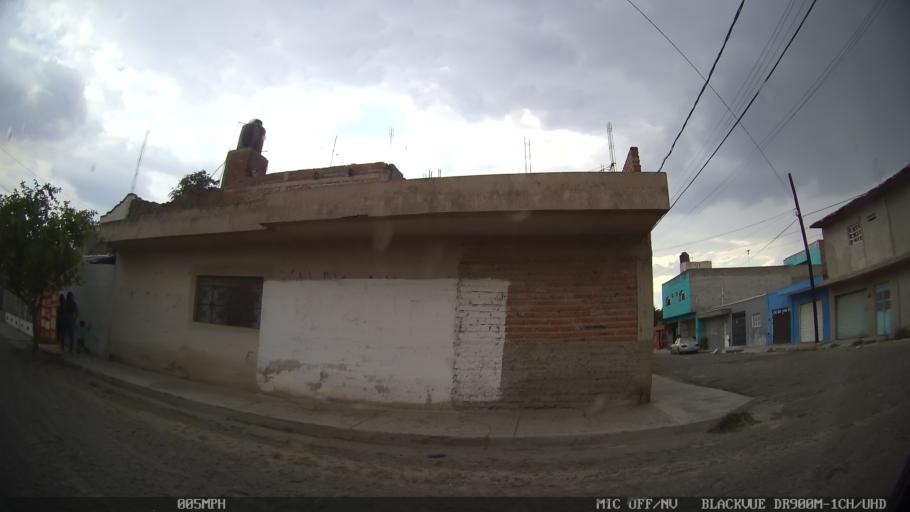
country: MX
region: Jalisco
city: Tlaquepaque
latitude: 20.6274
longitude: -103.2750
